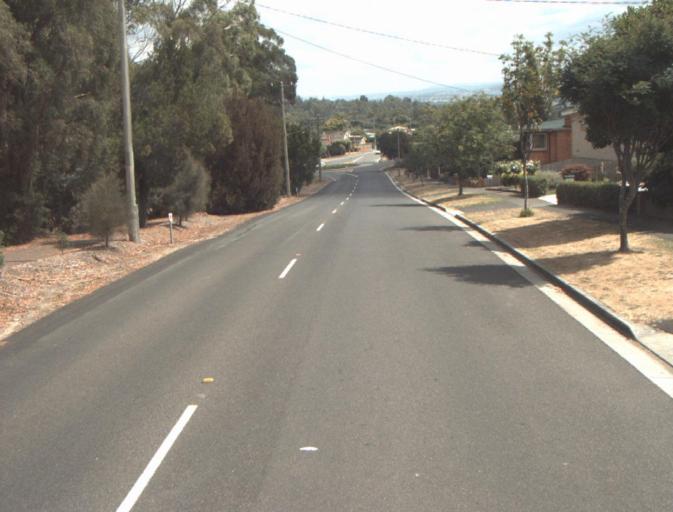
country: AU
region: Tasmania
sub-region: Launceston
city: Newstead
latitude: -41.4652
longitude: 147.1748
